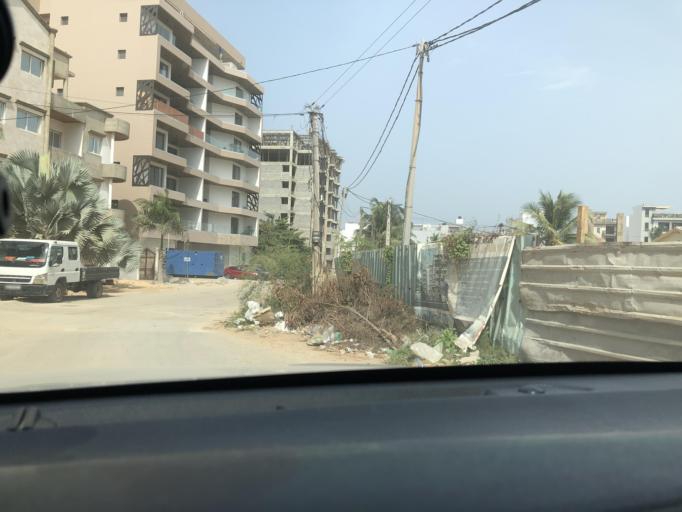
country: SN
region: Dakar
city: Mermoz Boabab
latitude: 14.7440
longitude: -17.5178
